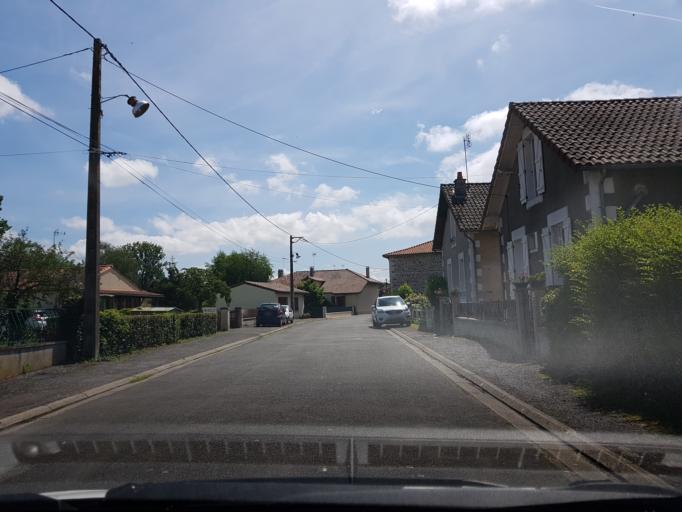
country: FR
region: Poitou-Charentes
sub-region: Departement de la Charente
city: Chabanais
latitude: 45.8751
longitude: 0.7121
